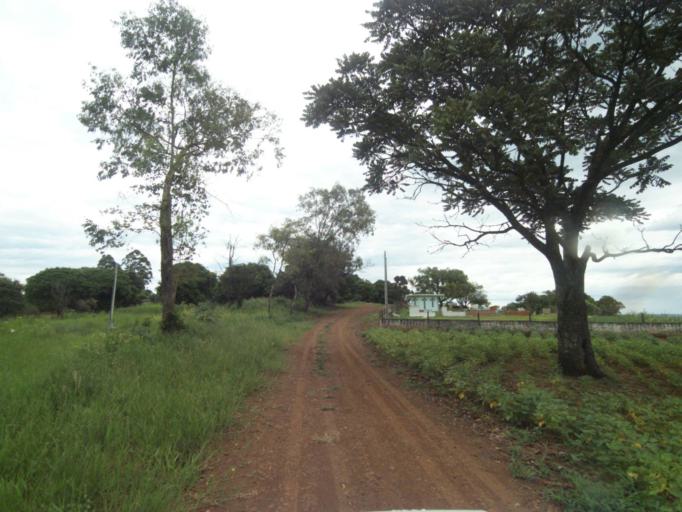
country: BR
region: Parana
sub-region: Guaraniacu
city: Guaraniacu
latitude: -24.9076
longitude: -52.9351
